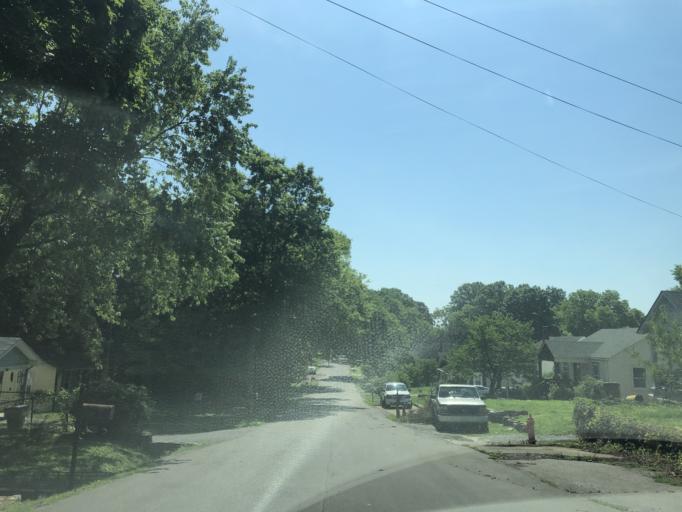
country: US
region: Tennessee
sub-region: Davidson County
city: Nashville
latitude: 36.2004
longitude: -86.7646
